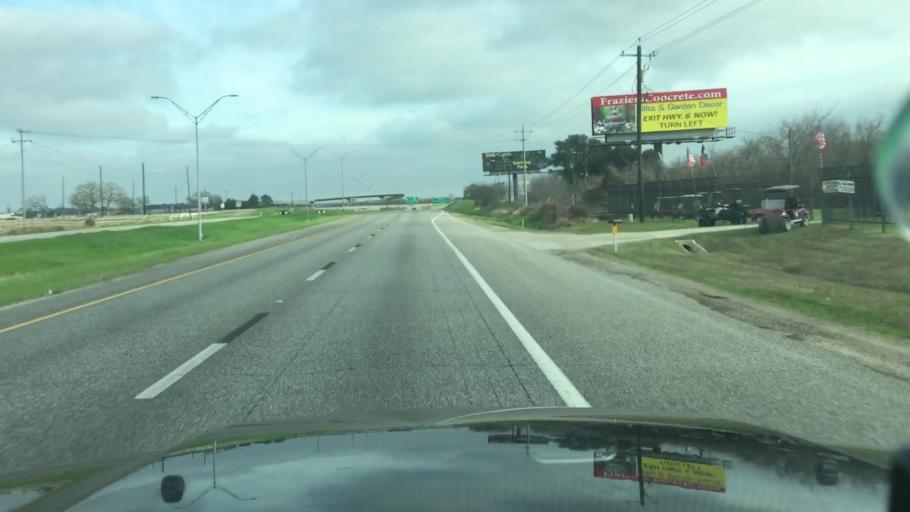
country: US
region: Texas
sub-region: Waller County
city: Hempstead
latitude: 30.1167
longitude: -96.0864
